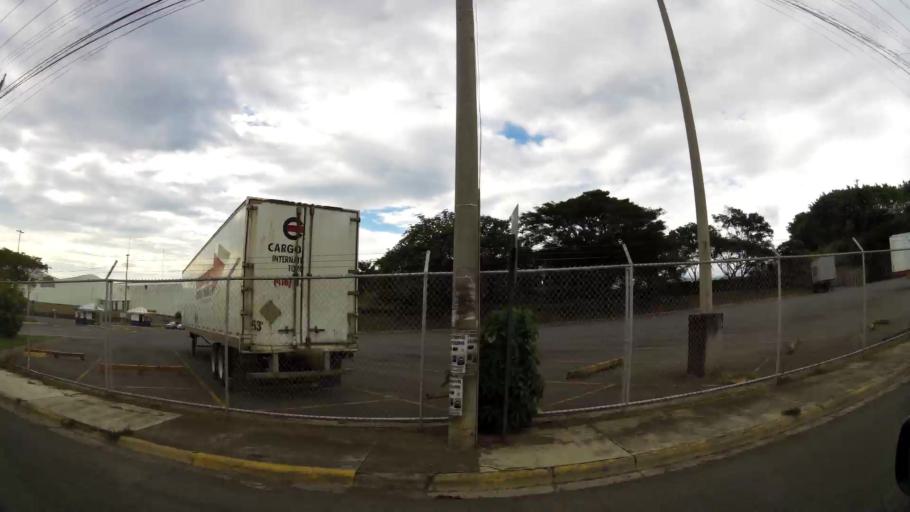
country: CR
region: Heredia
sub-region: Canton de Belen
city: San Antonio
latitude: 9.9676
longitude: -84.1892
